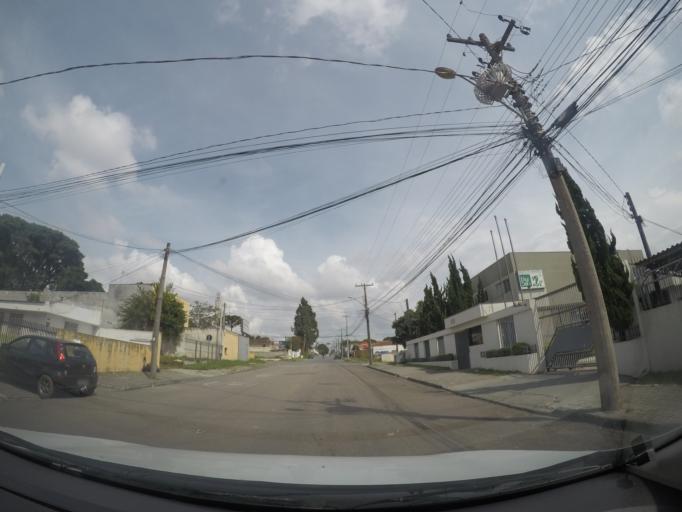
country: BR
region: Parana
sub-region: Curitiba
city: Curitiba
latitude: -25.4832
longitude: -49.2673
